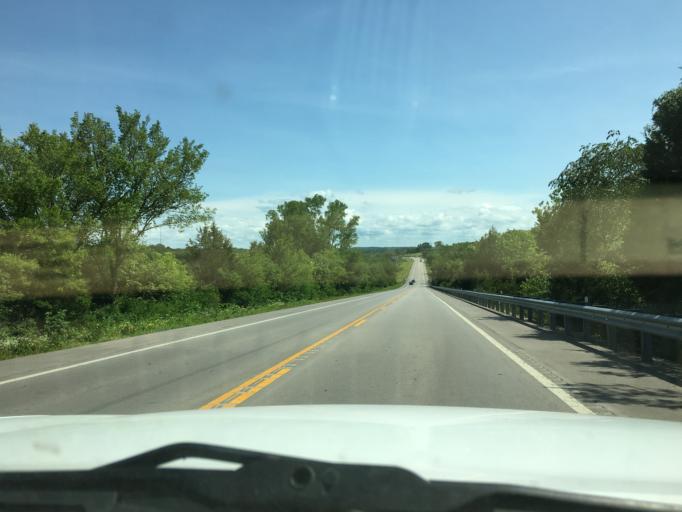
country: US
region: Missouri
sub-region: Franklin County
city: Union
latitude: 38.4687
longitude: -91.0056
